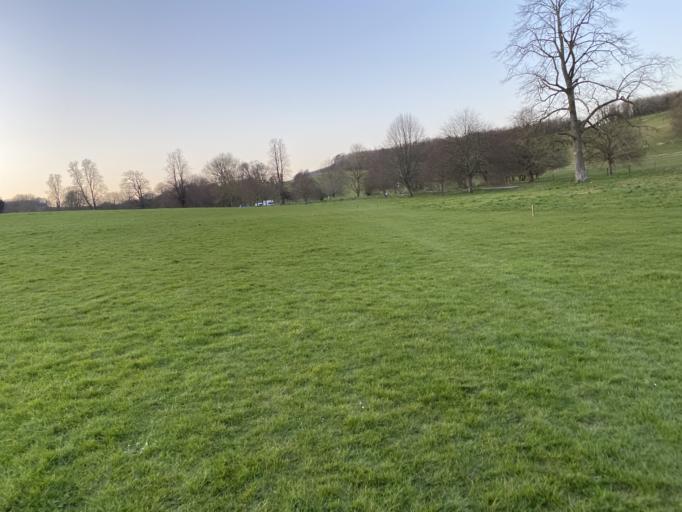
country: GB
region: England
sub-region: Brighton and Hove
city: Brighton
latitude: 50.8659
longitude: -0.0973
